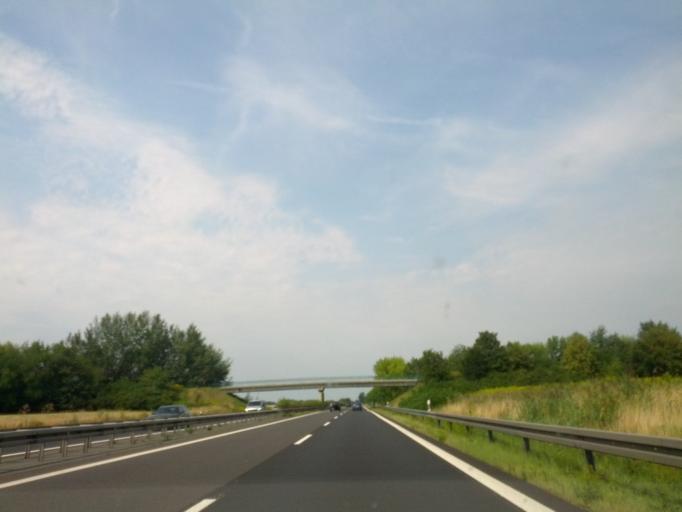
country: DE
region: Brandenburg
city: Wustermark
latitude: 52.4879
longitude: 12.9638
